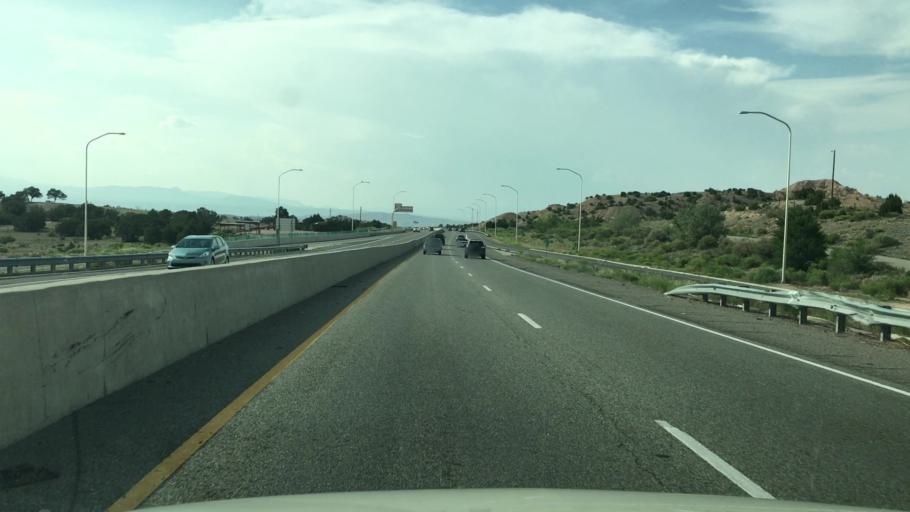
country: US
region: New Mexico
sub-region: Santa Fe County
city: Nambe
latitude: 35.8234
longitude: -105.9768
